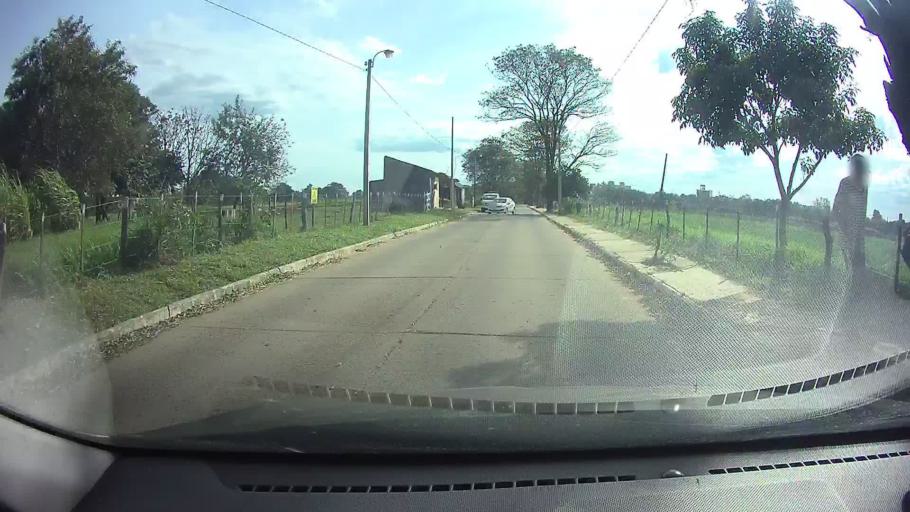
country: PY
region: Central
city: Fernando de la Mora
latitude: -25.3296
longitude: -57.5239
